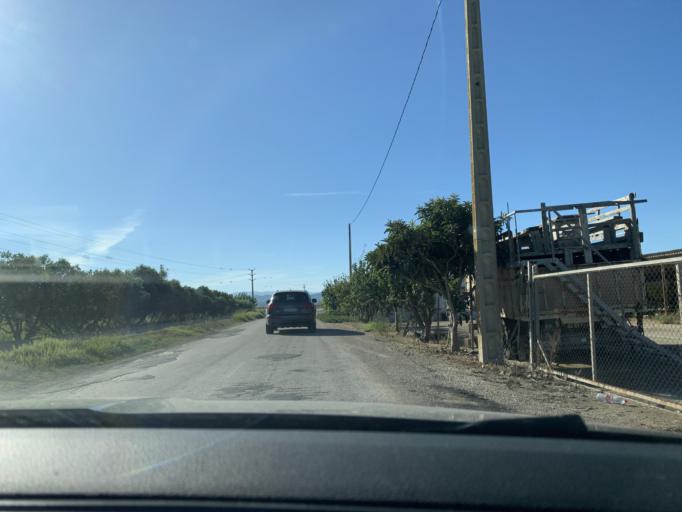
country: ES
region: Catalonia
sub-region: Provincia de Tarragona
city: Deltebre
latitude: 40.7483
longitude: 0.7279
